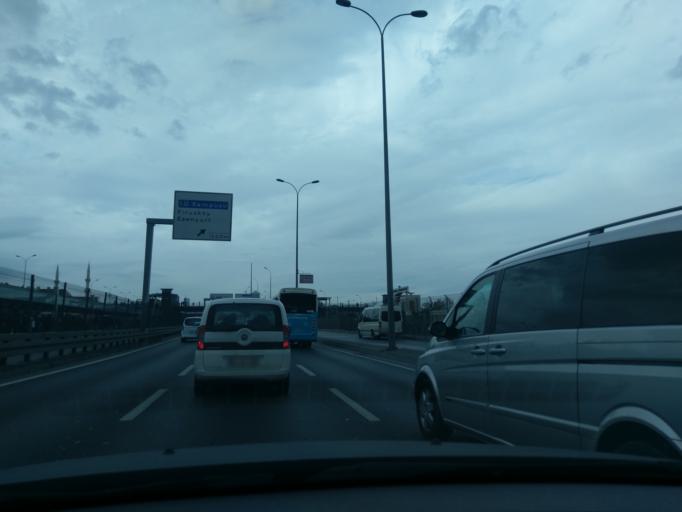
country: TR
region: Istanbul
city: Yakuplu
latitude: 40.9831
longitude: 28.7271
